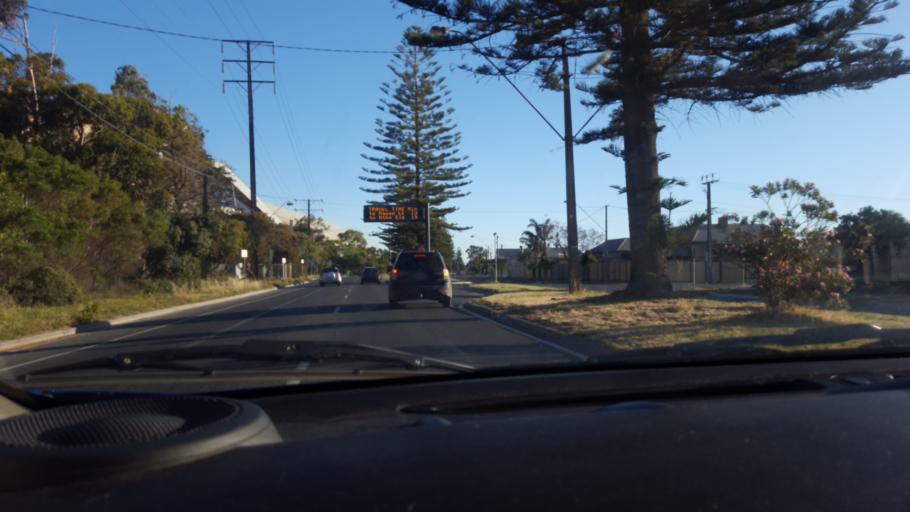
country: AU
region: South Australia
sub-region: Port Adelaide Enfield
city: Birkenhead
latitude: -34.8323
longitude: 138.5016
